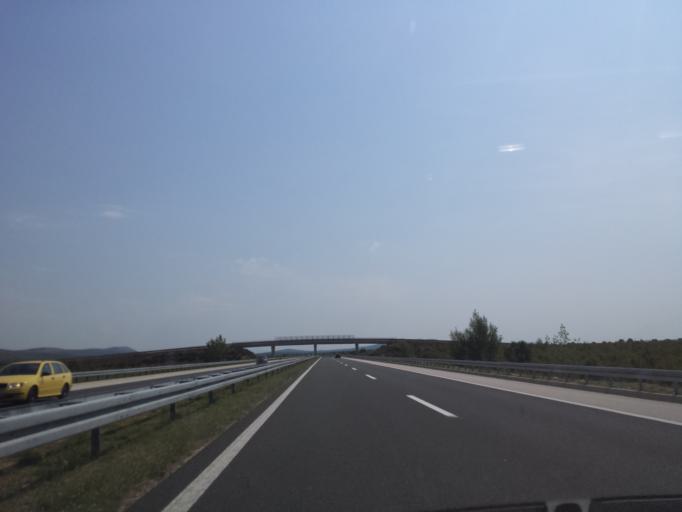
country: HR
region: Zadarska
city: Benkovac
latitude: 43.9755
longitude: 15.6426
